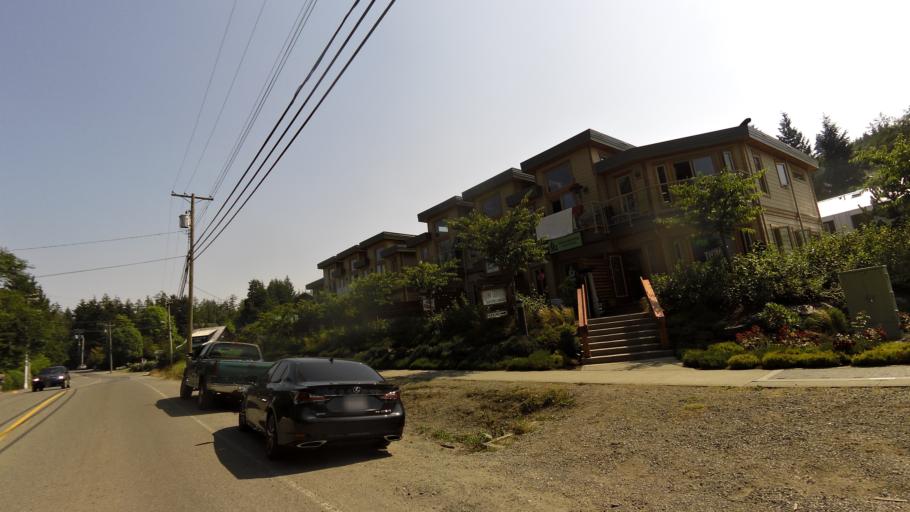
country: CA
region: British Columbia
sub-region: Regional District of Alberni-Clayoquot
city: Tofino
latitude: 49.1506
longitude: -125.8980
